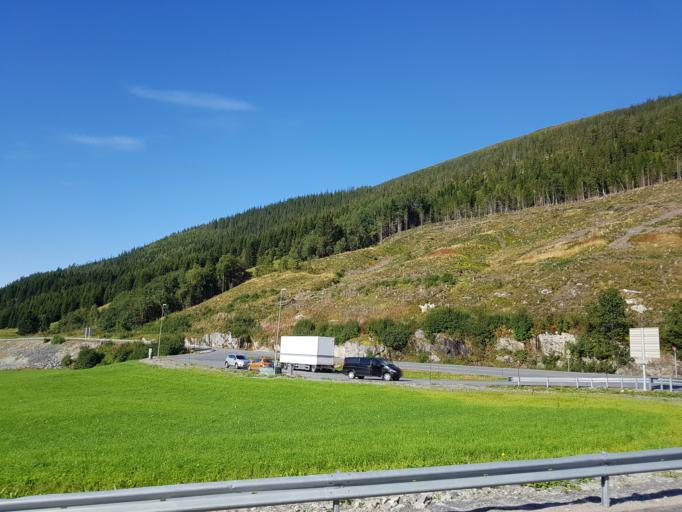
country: NO
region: Sor-Trondelag
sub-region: Rissa
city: Rissa
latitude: 63.6730
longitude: 10.2124
